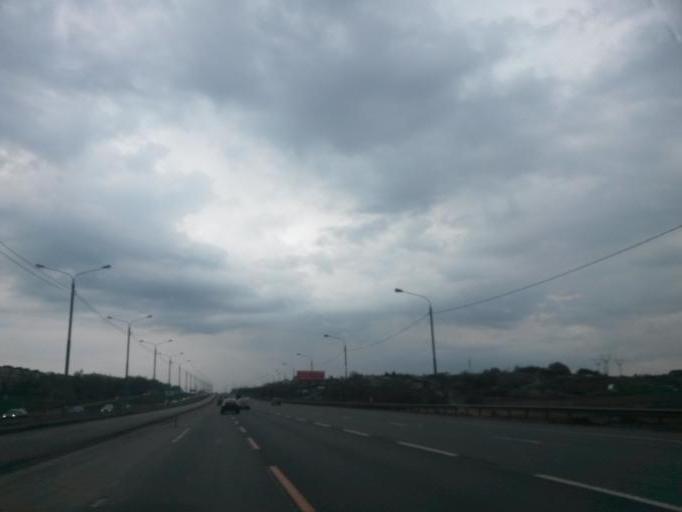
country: RU
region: Moskovskaya
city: Shcherbinka
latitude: 55.4679
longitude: 37.6182
